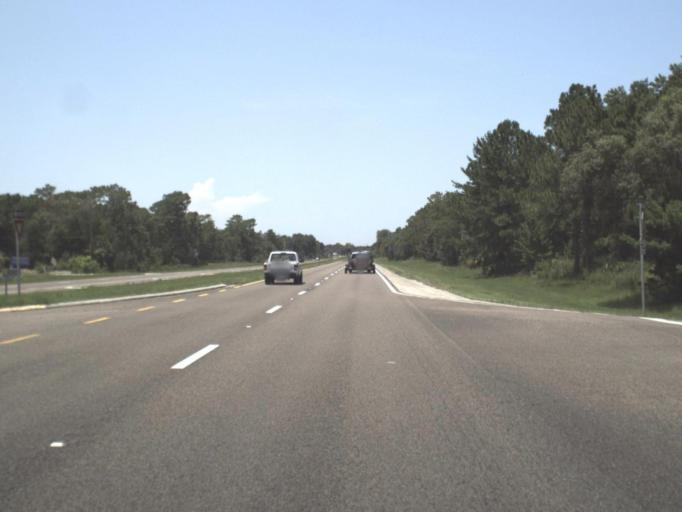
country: US
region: Florida
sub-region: Citrus County
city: Sugarmill Woods
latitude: 28.7164
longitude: -82.5412
